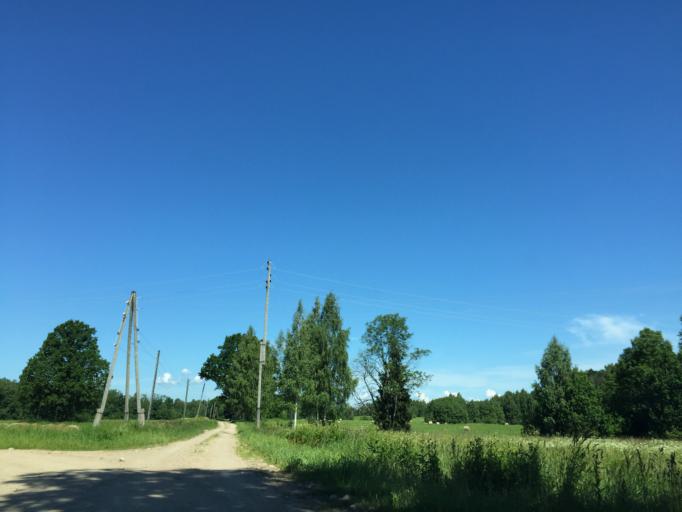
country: LV
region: Sigulda
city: Sigulda
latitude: 57.2221
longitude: 24.9342
